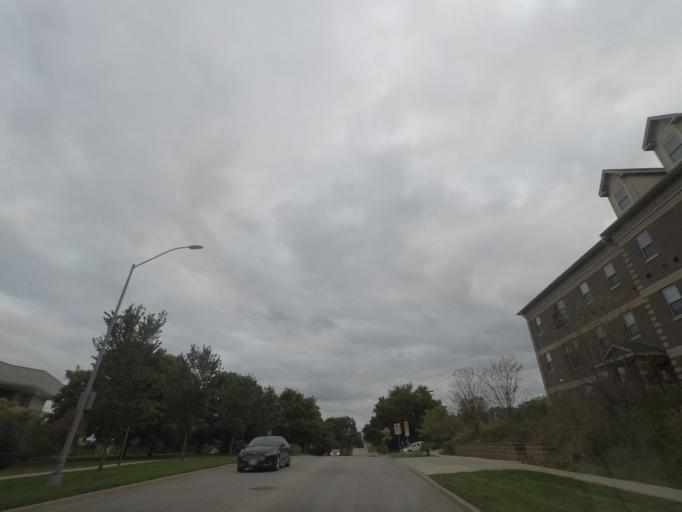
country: US
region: Iowa
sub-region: Story County
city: Ames
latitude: 42.0211
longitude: -93.6395
